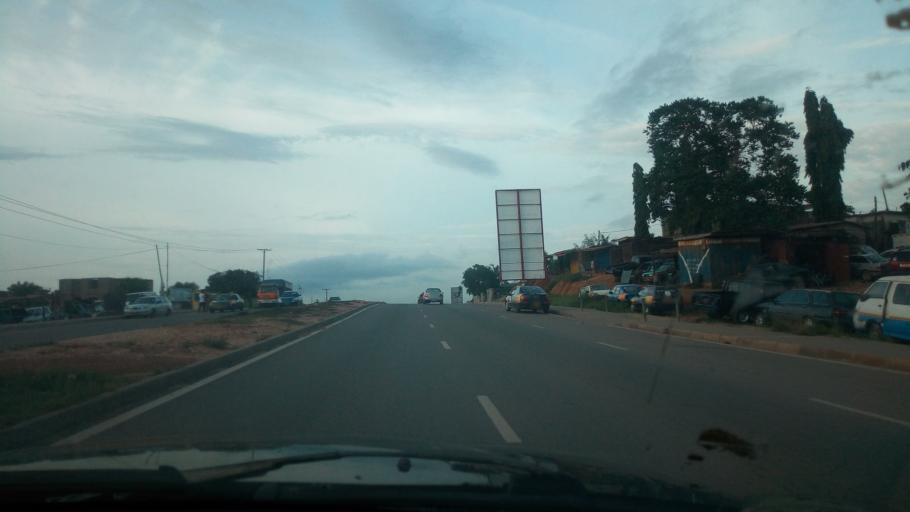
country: GH
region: Western
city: Takoradi
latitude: 4.9197
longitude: -1.7880
